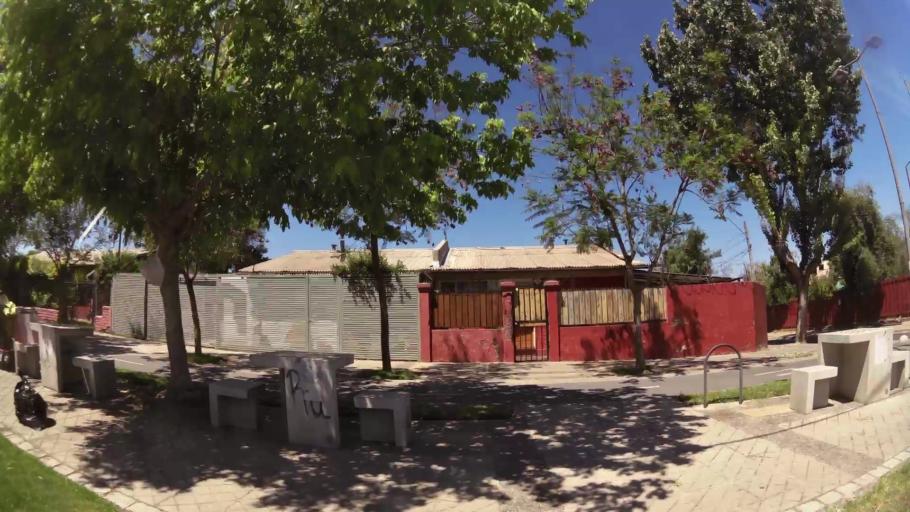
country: CL
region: Santiago Metropolitan
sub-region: Provincia de Maipo
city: San Bernardo
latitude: -33.5696
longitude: -70.6790
